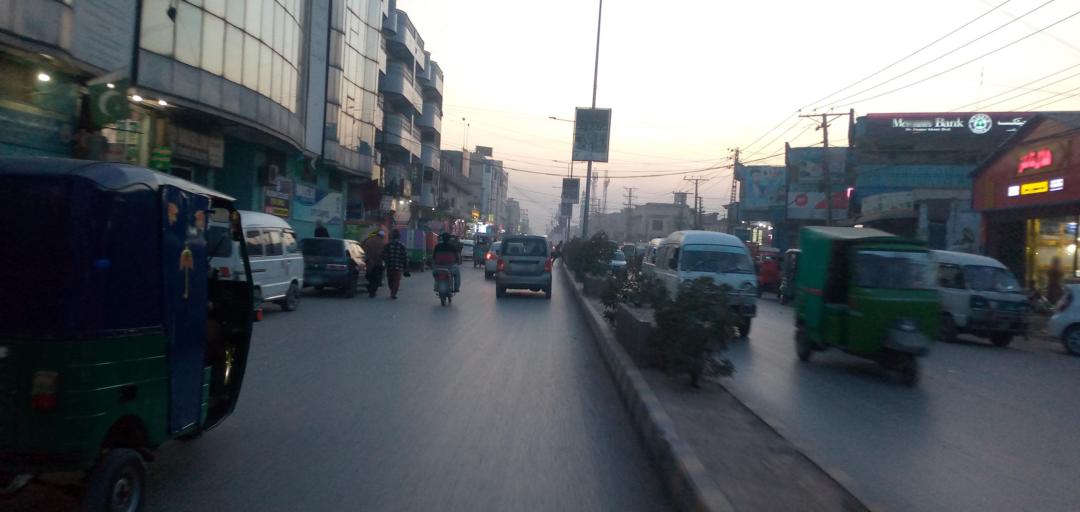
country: PK
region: Khyber Pakhtunkhwa
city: Peshawar
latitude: 34.0277
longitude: 71.5994
